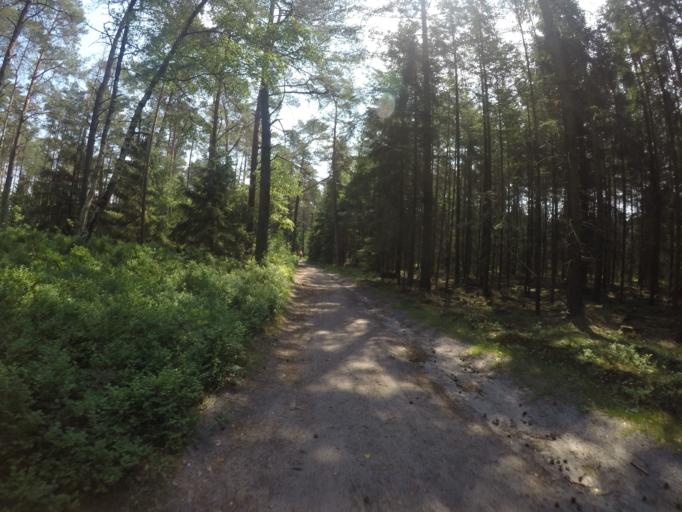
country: DE
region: Lower Saxony
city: Buchholz in der Nordheide
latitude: 53.2951
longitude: 9.8354
